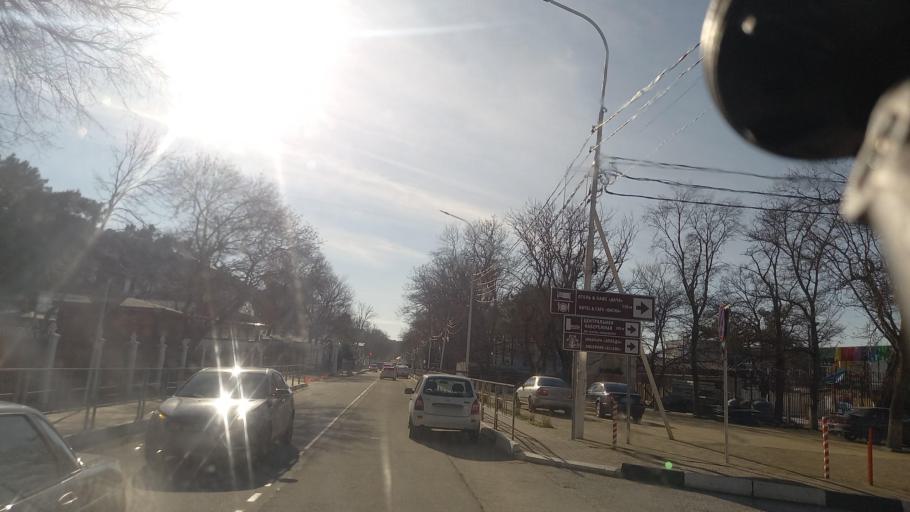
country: RU
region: Krasnodarskiy
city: Kabardinka
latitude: 44.6464
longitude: 37.9341
